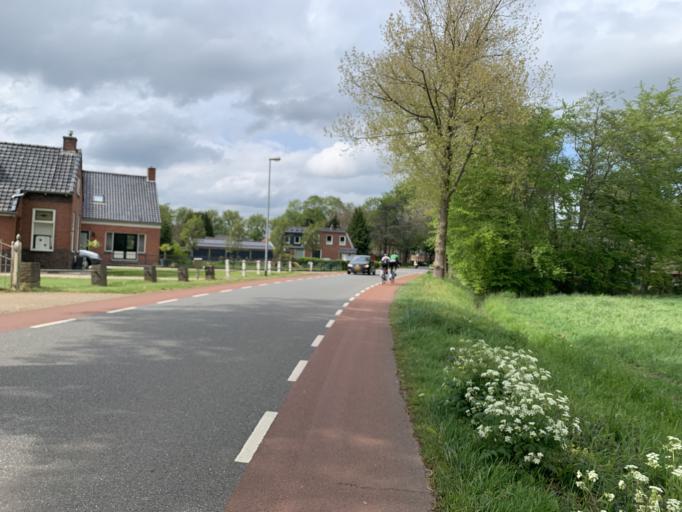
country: NL
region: Groningen
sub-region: Gemeente Haren
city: Haren
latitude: 53.2130
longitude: 6.6417
